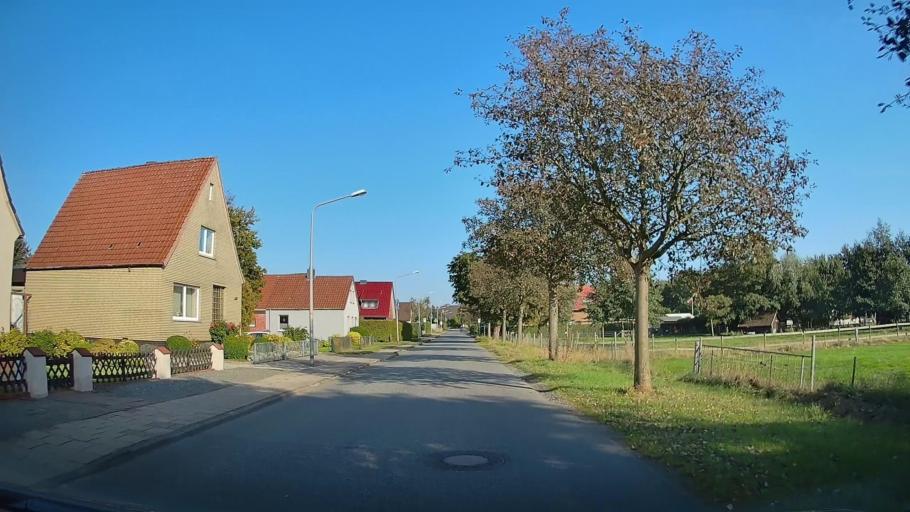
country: DE
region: Lower Saxony
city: Cuxhaven
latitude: 53.8512
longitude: 8.6582
